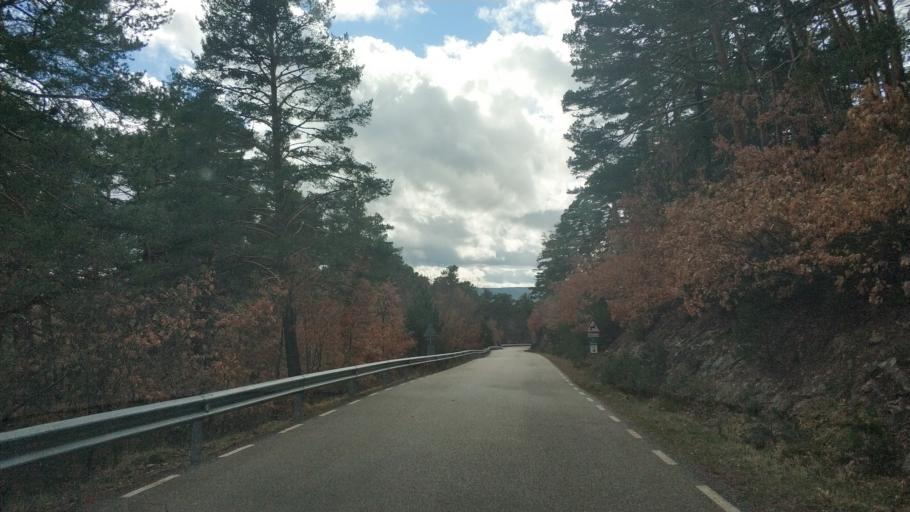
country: ES
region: Castille and Leon
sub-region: Provincia de Burgos
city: Quintanar de la Sierra
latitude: 41.9995
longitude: -3.0162
